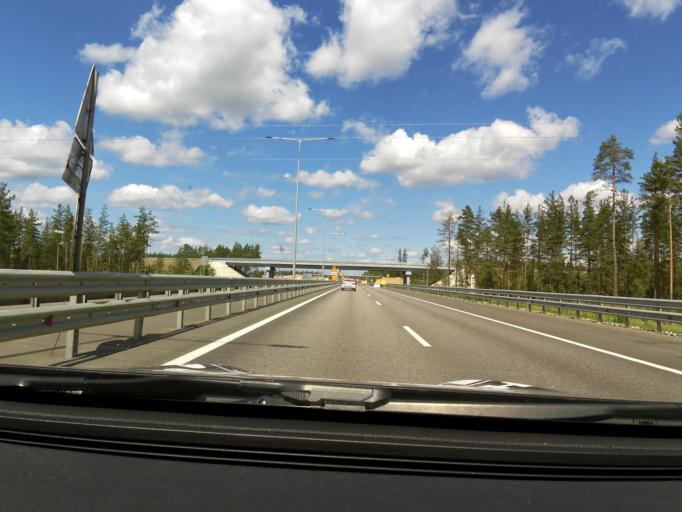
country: RU
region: Tverskaya
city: Bologoye
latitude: 57.6977
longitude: 34.2075
